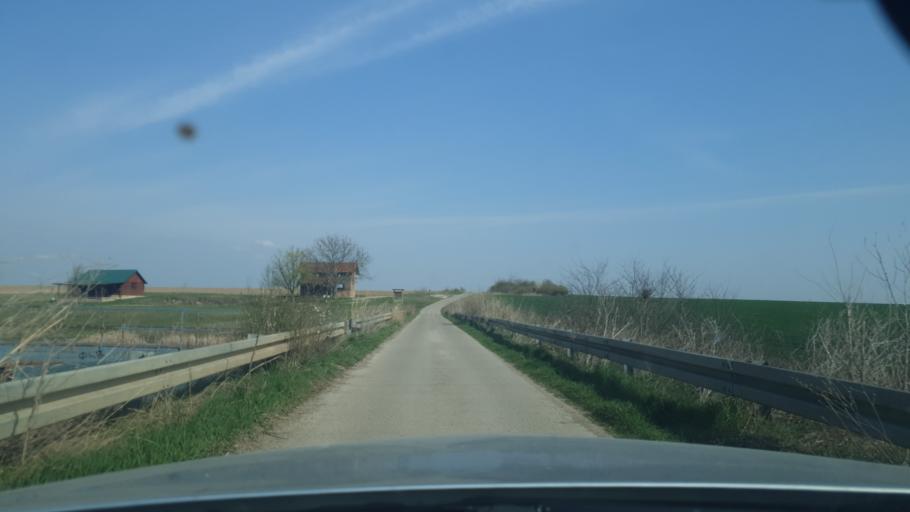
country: RS
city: Putinci
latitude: 45.0443
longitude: 19.9426
